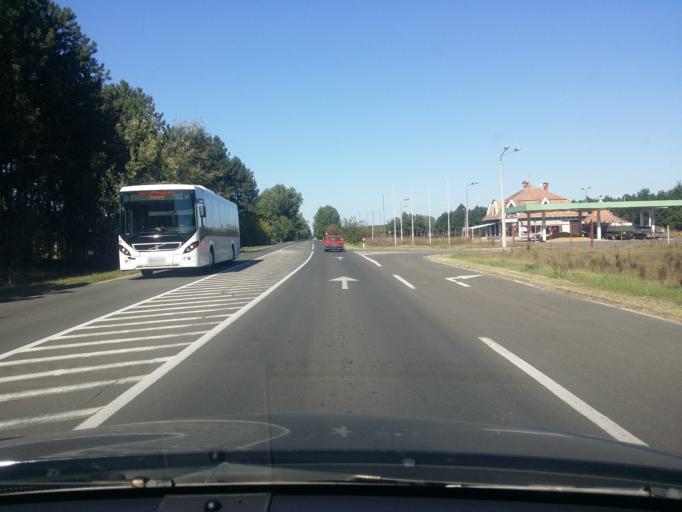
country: HU
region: Csongrad
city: Pusztaszer
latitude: 46.5376
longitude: 19.9581
